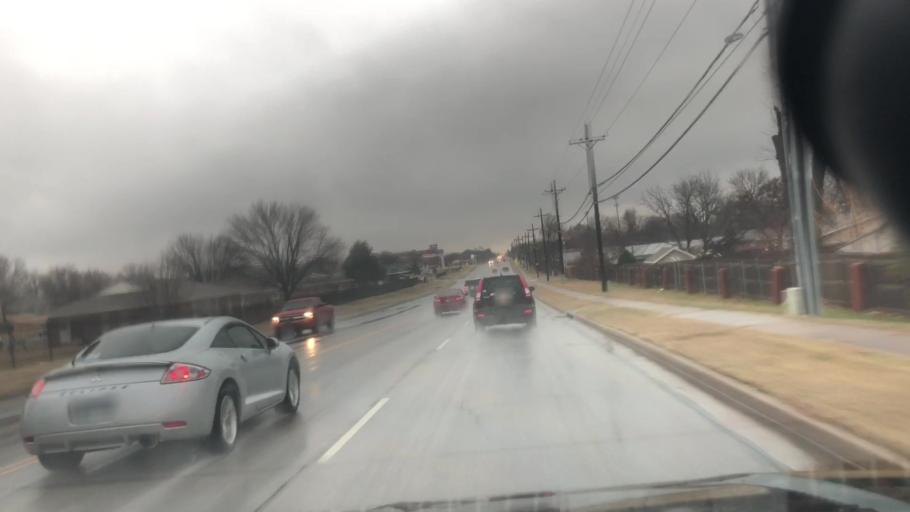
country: US
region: Oklahoma
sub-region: Tulsa County
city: Broken Arrow
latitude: 36.1405
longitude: -95.8333
